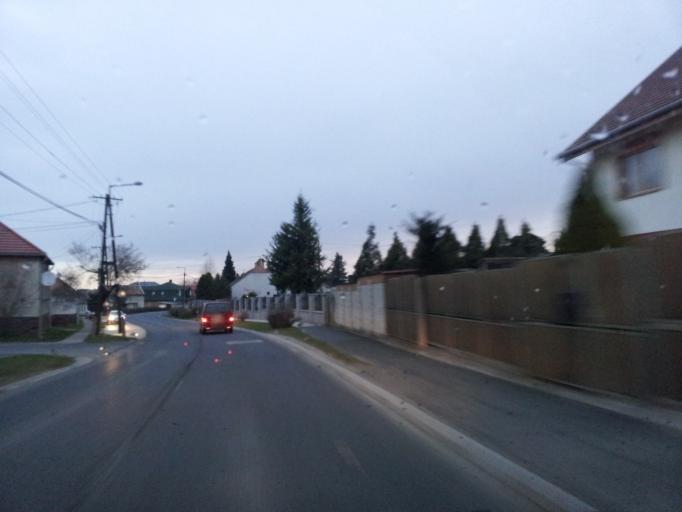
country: HU
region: Gyor-Moson-Sopron
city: Fertoszentmiklos
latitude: 47.5856
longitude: 16.8808
